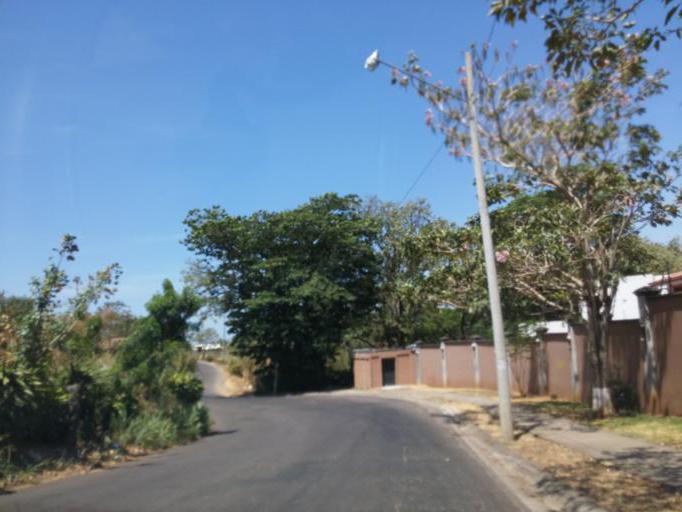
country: CR
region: Alajuela
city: Alajuela
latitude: 10.0165
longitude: -84.2277
